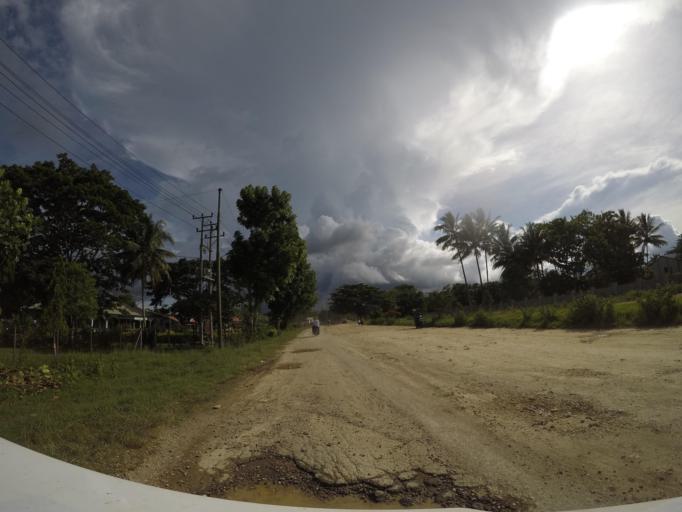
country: TL
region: Lautem
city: Lospalos
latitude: -8.4937
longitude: 126.9926
